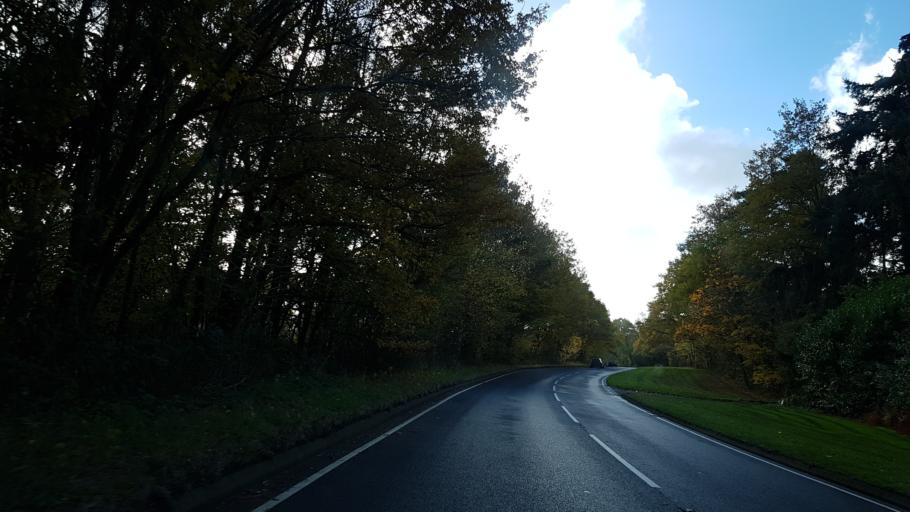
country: GB
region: England
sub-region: Surrey
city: Milford
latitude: 51.1286
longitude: -0.6722
